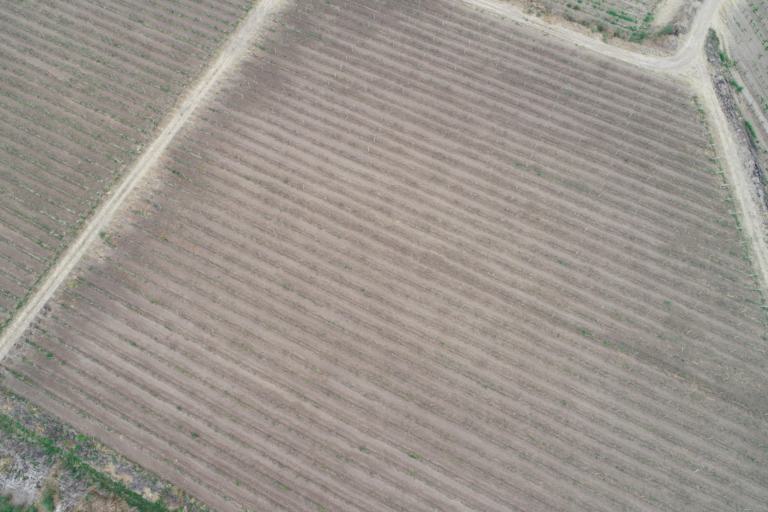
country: BO
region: Tarija
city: Tarija
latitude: -21.6000
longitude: -64.6208
